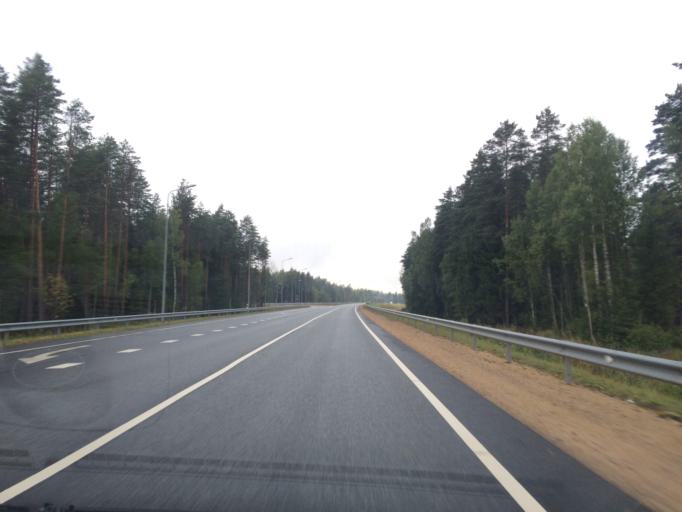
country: LV
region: Ogre
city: Ogre
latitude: 56.8419
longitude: 24.6837
